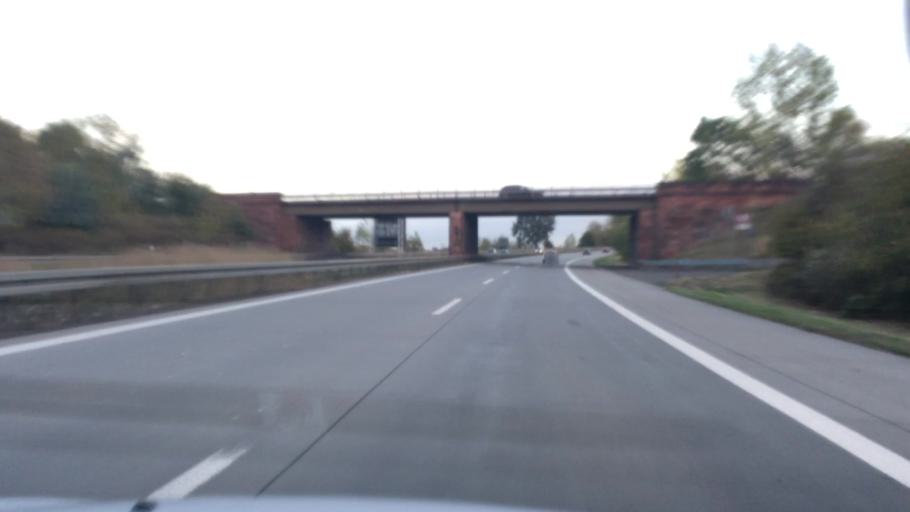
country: DE
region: Saxony
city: Borsdorf
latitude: 51.3504
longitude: 12.5027
